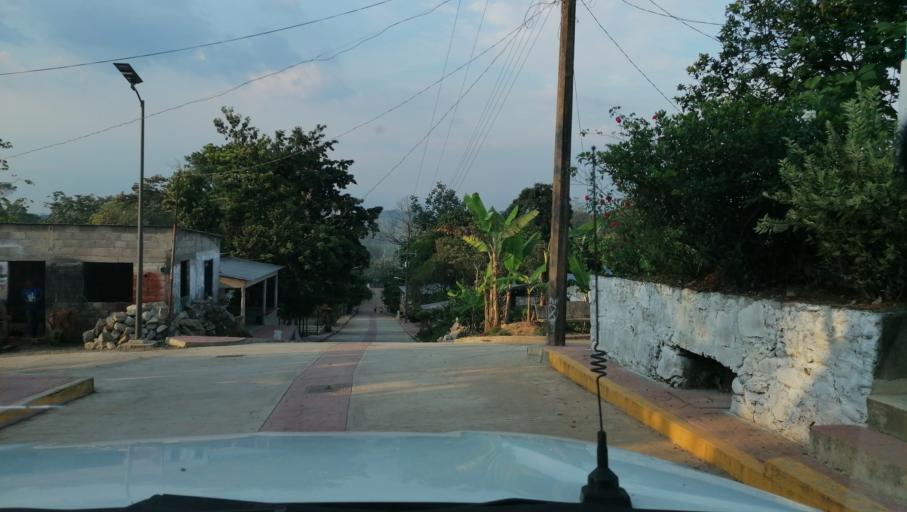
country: MX
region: Chiapas
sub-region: Juarez
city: El Triunfo 1ra. Seccion (Cardona)
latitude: 17.4916
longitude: -93.2433
